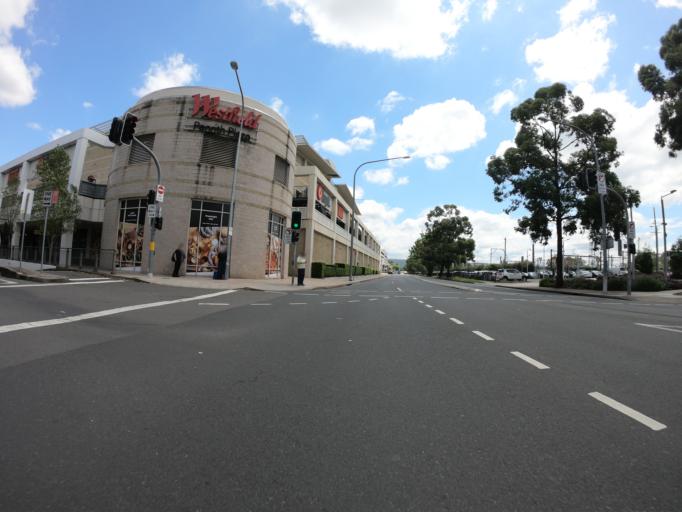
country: AU
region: New South Wales
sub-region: Penrith Municipality
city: Penrith
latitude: -33.7505
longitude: 150.6945
